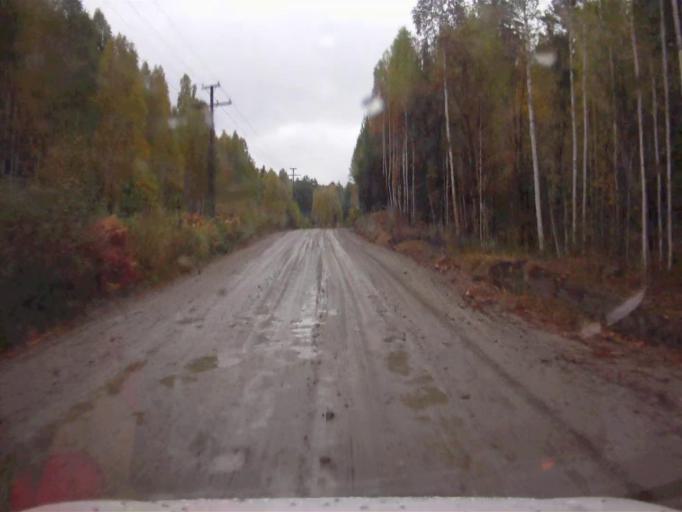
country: RU
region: Chelyabinsk
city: Kyshtym
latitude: 55.7983
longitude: 60.4808
